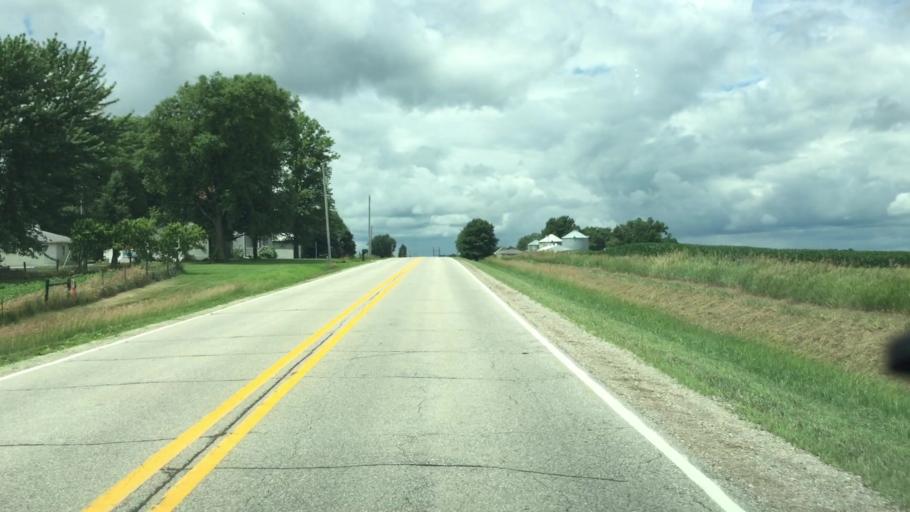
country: US
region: Iowa
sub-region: Jasper County
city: Monroe
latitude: 41.5736
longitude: -93.0853
